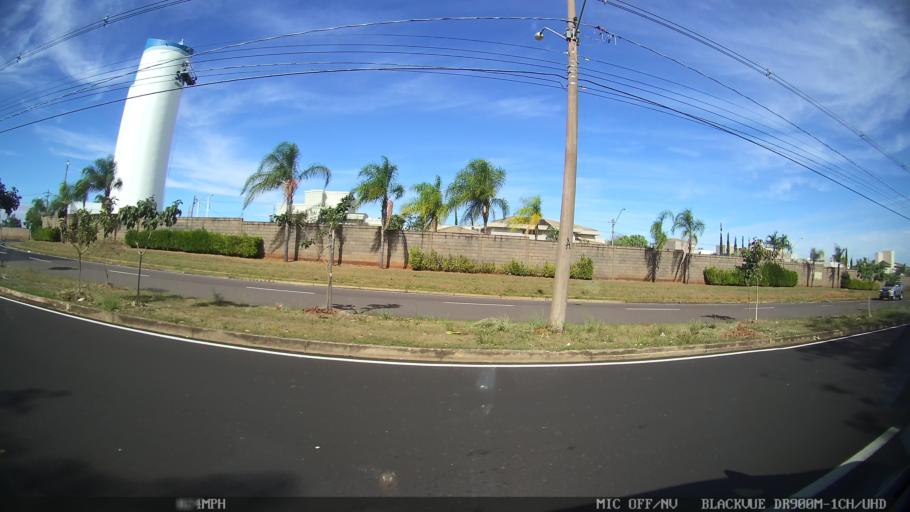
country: BR
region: Sao Paulo
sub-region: Sao Jose Do Rio Preto
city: Sao Jose do Rio Preto
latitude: -20.8076
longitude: -49.3332
